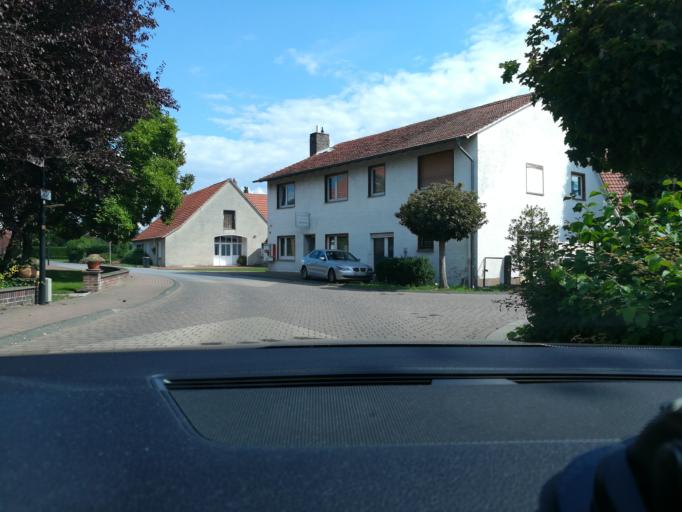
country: DE
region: North Rhine-Westphalia
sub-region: Regierungsbezirk Detmold
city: Hille
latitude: 52.3330
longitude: 8.7365
